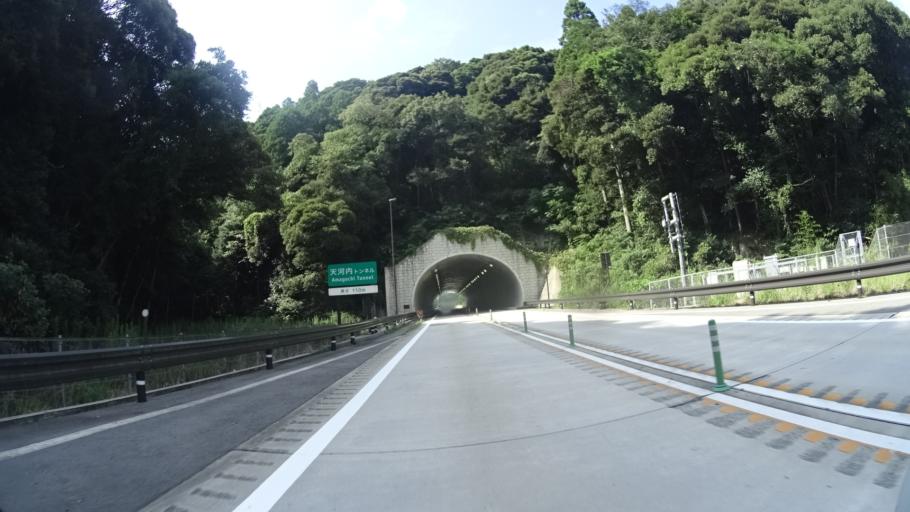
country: JP
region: Shimane
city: Odacho-oda
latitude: 35.1373
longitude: 132.4065
